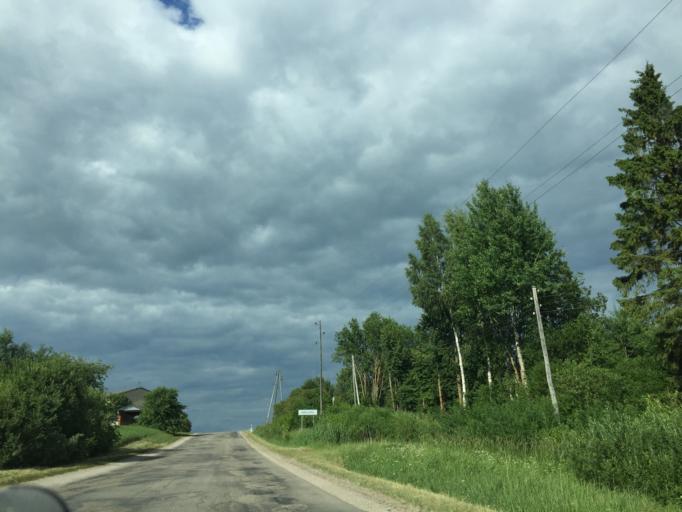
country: LV
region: Skriveri
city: Skriveri
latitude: 56.8412
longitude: 25.1443
